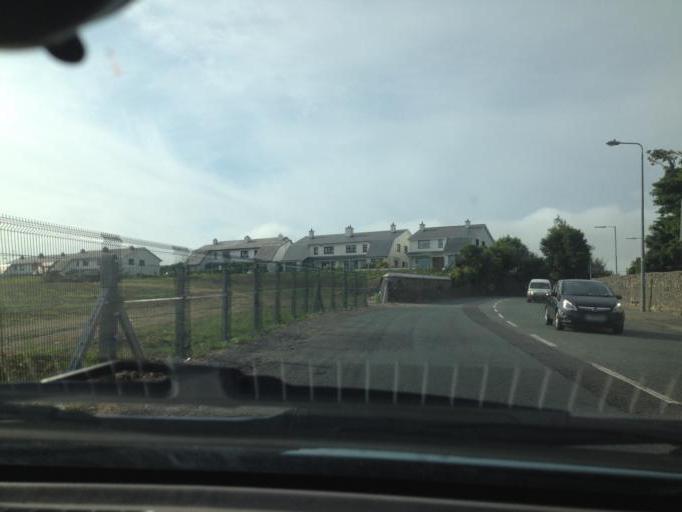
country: IE
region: Connaught
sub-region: Sligo
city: Sligo
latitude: 54.2824
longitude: -8.4757
